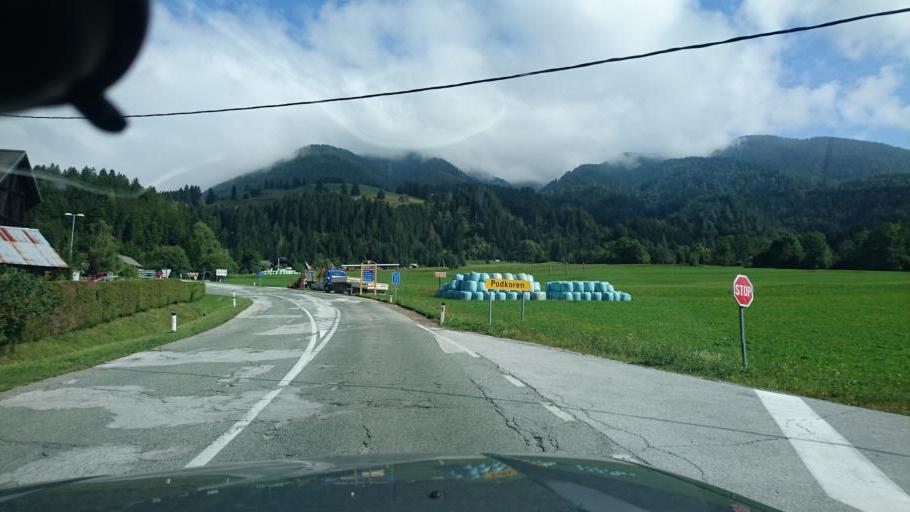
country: SI
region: Kranjska Gora
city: Kranjska Gora
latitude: 46.4924
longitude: 13.7583
